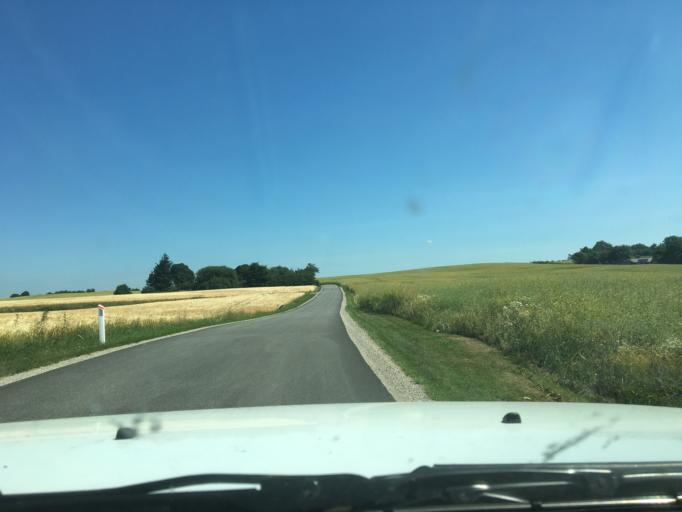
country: DK
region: Central Jutland
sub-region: Horsens Kommune
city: Braedstrup
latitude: 55.9524
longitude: 9.5723
